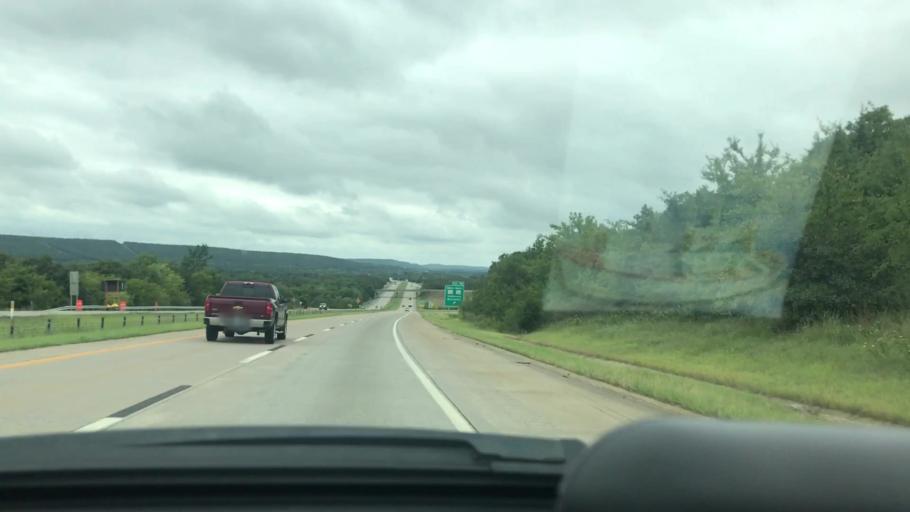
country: US
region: Oklahoma
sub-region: Pittsburg County
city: Krebs
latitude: 34.9931
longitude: -95.7214
